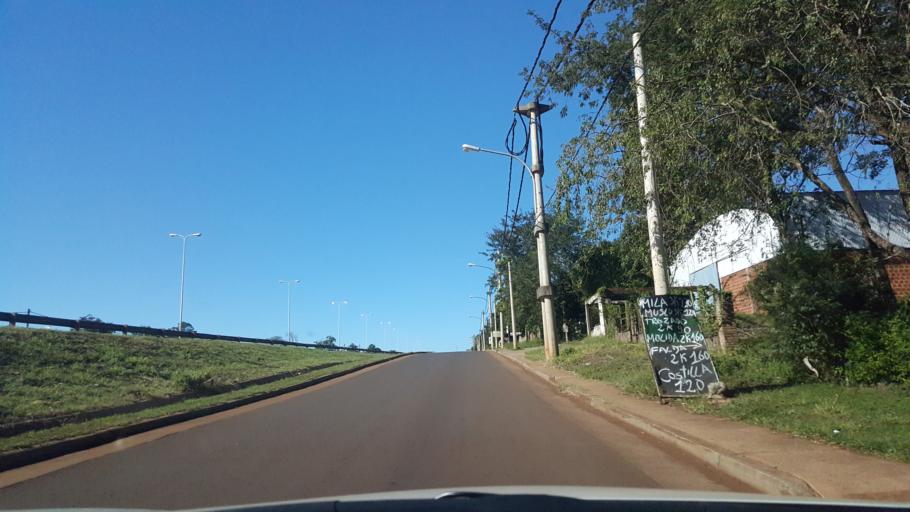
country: AR
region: Misiones
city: Garupa
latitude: -27.4610
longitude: -55.8372
